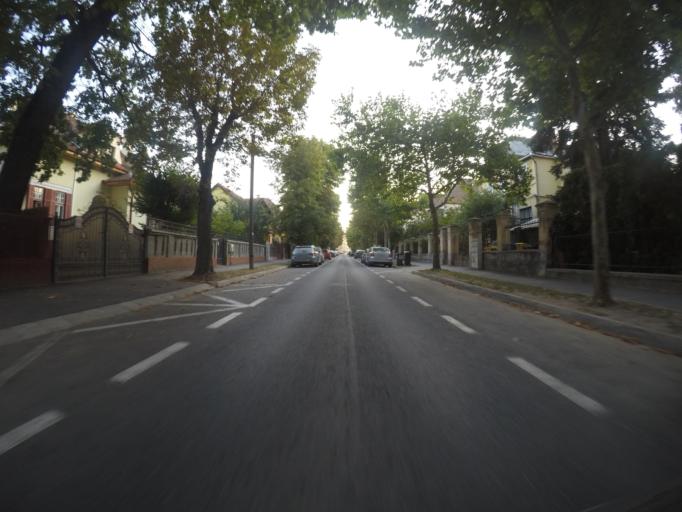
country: RO
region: Sibiu
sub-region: Municipiul Sibiu
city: Sibiu
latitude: 45.7912
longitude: 24.1544
